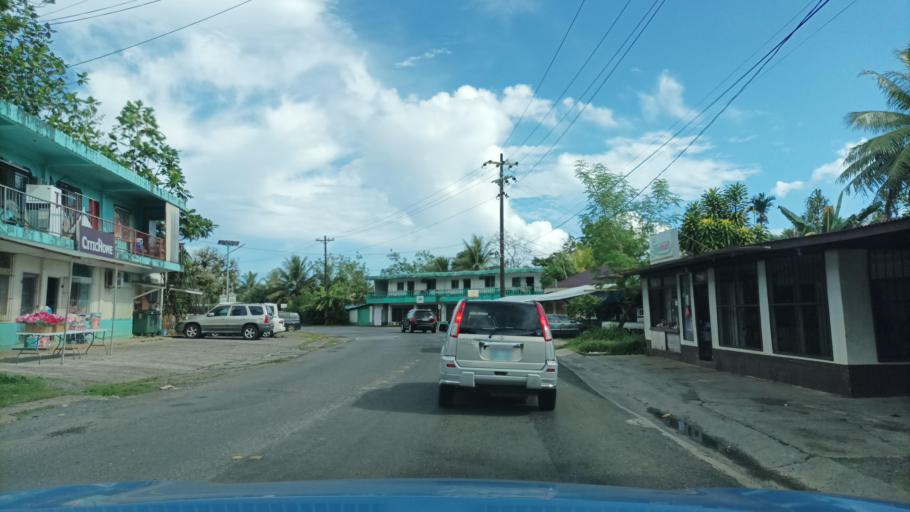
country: FM
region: Pohnpei
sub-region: Kolonia Municipality
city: Kolonia
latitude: 6.9637
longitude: 158.2148
